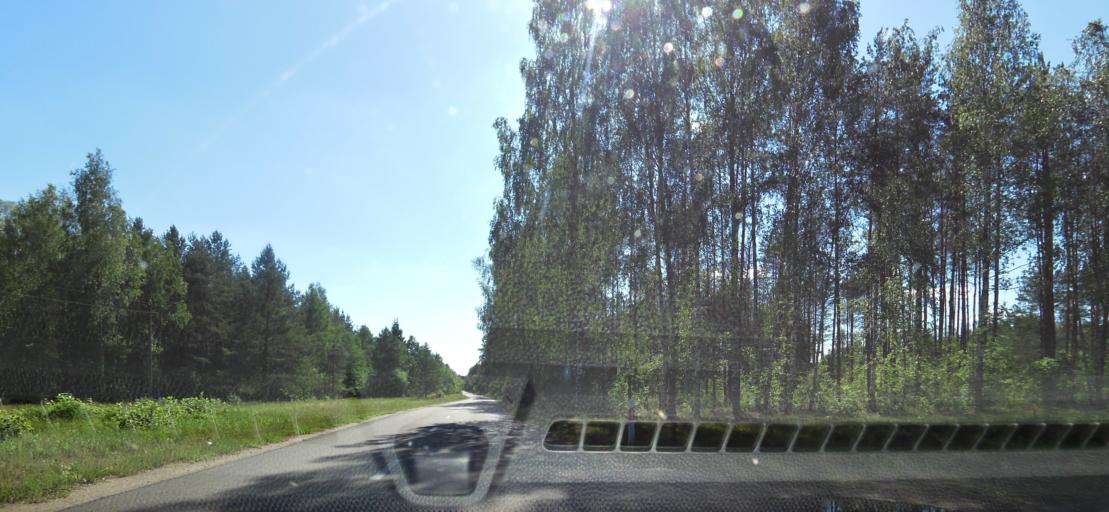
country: LT
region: Vilnius County
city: Rasos
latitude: 54.7570
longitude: 25.3403
